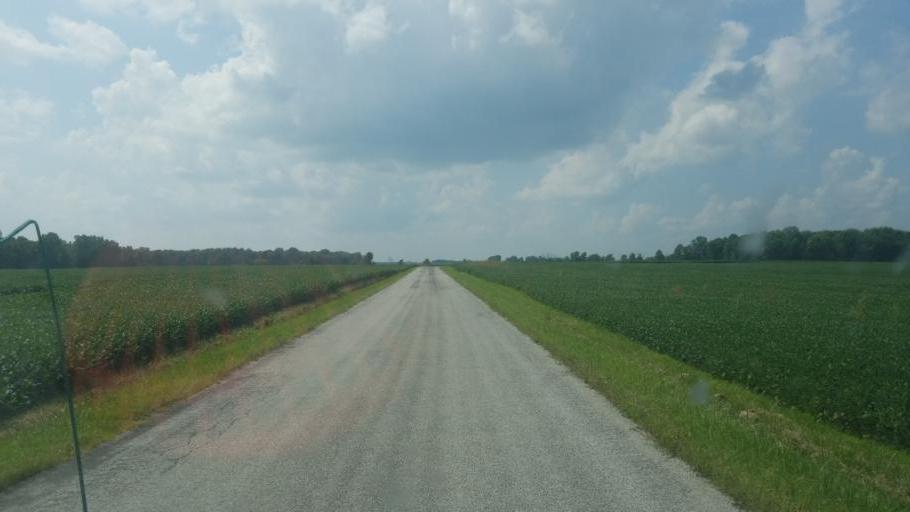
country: US
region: Ohio
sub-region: Huron County
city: New London
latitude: 40.9872
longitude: -82.4211
